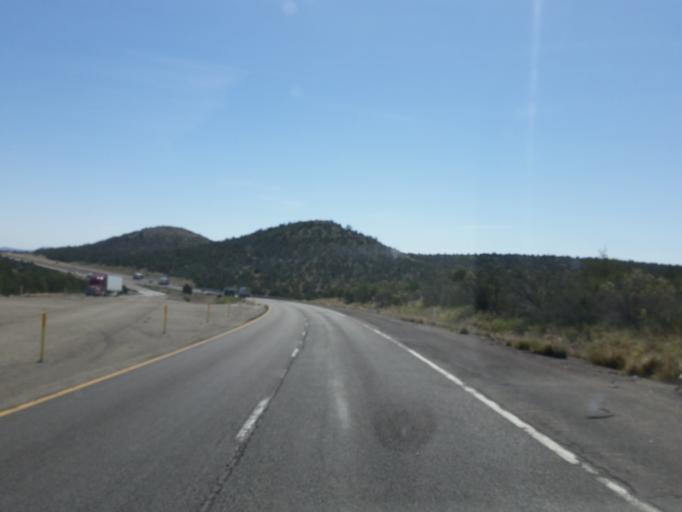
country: US
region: Arizona
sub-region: Mohave County
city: Peach Springs
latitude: 35.2927
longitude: -113.0333
